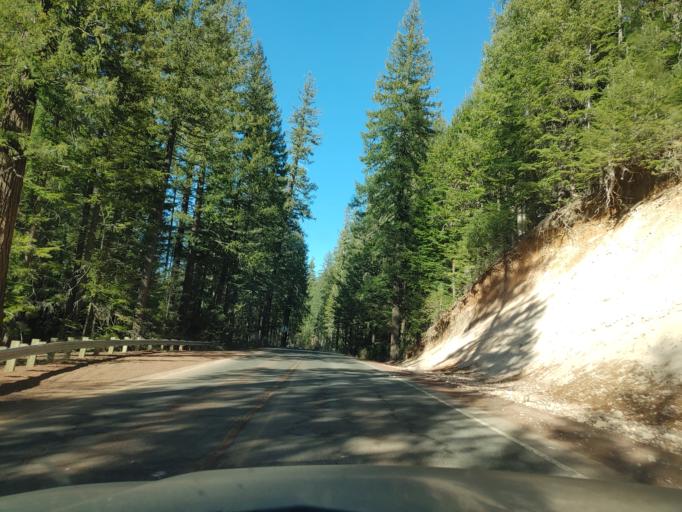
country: US
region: Oregon
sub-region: Jackson County
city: Shady Cove
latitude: 42.9257
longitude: -122.4261
